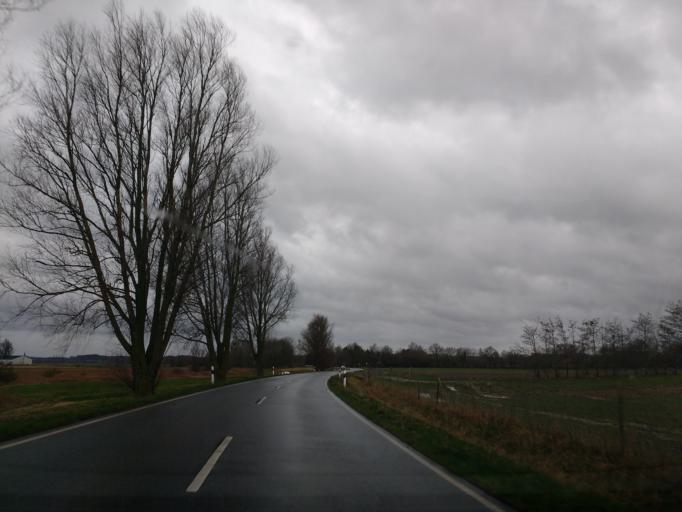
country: DE
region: Schleswig-Holstein
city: Blekendorf
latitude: 54.3116
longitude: 10.6565
